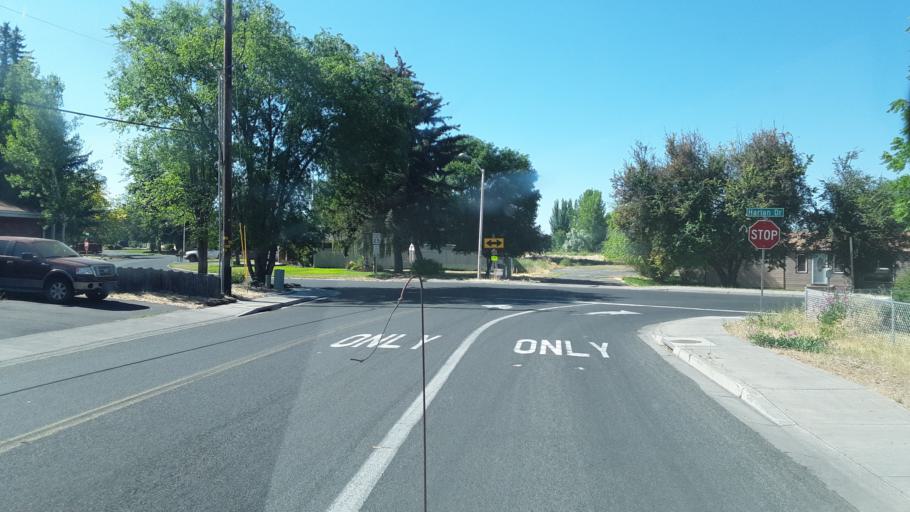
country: US
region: Oregon
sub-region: Klamath County
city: Altamont
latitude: 42.1917
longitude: -121.7178
